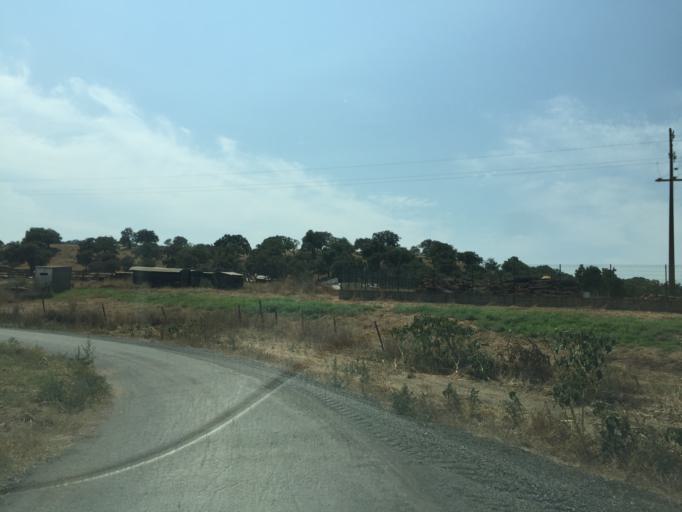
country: PT
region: Setubal
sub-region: Grandola
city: Grandola
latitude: 38.1342
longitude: -8.5031
